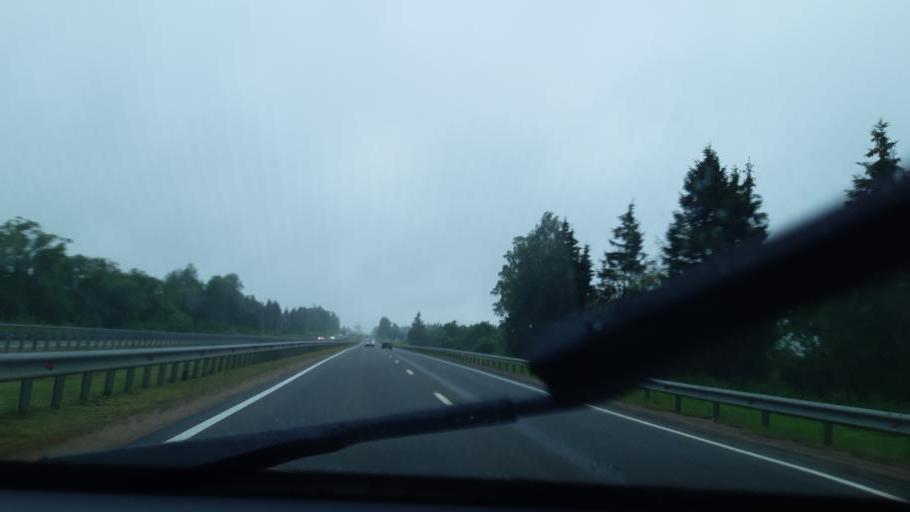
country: RU
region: Smolensk
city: Talashkino
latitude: 54.6667
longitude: 32.1535
